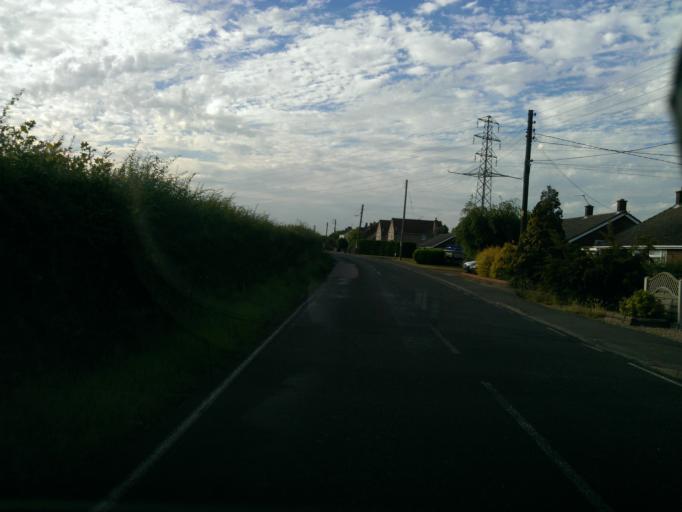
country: GB
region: England
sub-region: Essex
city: Great Bentley
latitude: 51.8402
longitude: 1.0704
